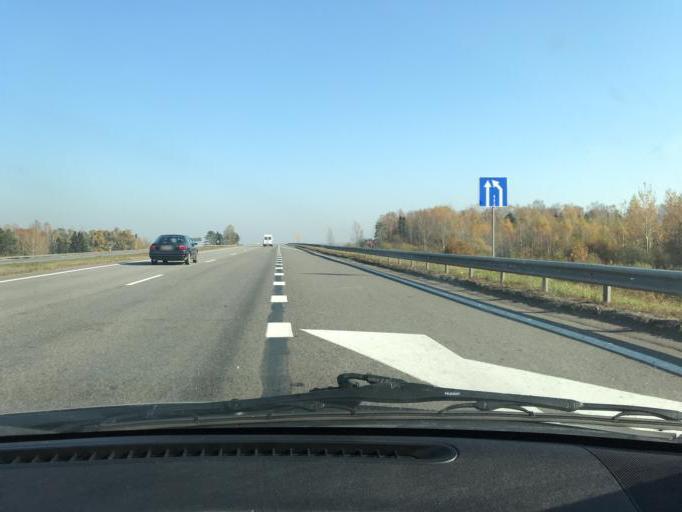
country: BY
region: Vitebsk
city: Baran'
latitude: 54.5582
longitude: 30.2821
